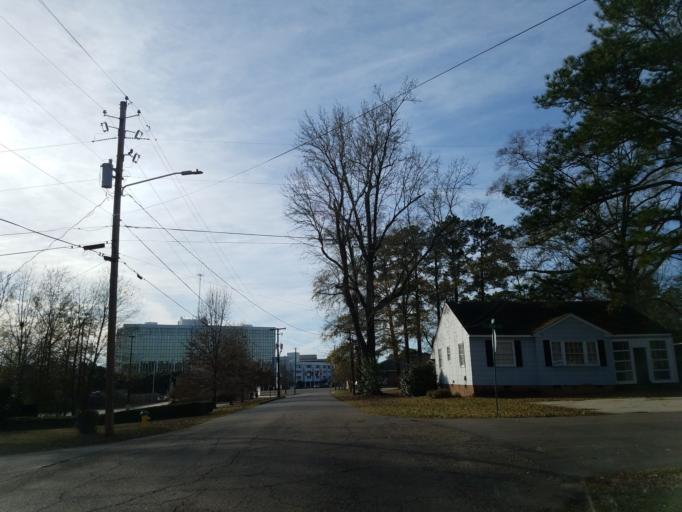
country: US
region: Mississippi
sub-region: Forrest County
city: Hattiesburg
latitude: 31.3193
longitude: -89.3262
